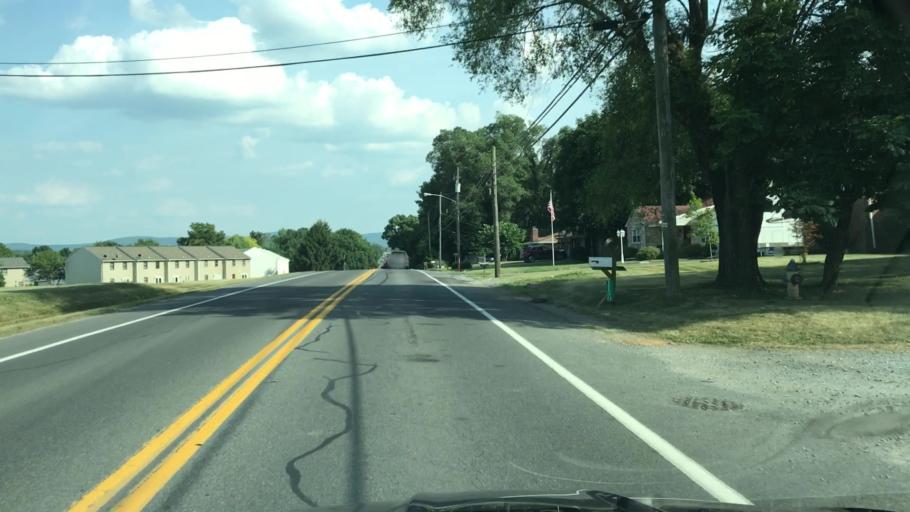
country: US
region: Pennsylvania
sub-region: Cumberland County
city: Carlisle
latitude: 40.1886
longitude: -77.1599
